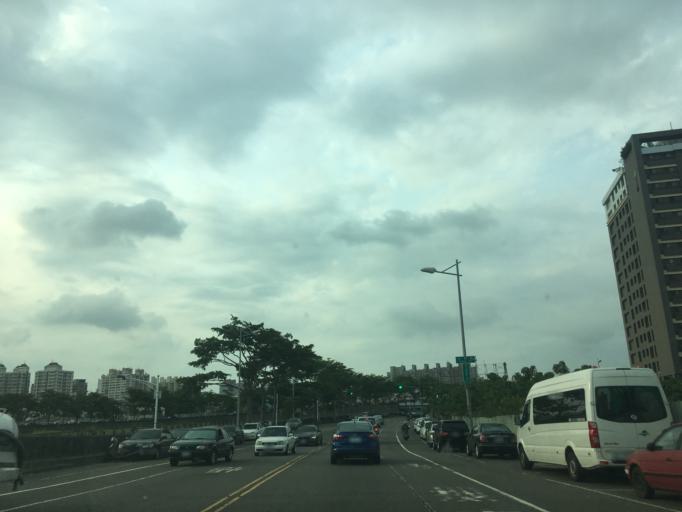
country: TW
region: Taiwan
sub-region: Taichung City
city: Taichung
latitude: 24.1614
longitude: 120.7047
